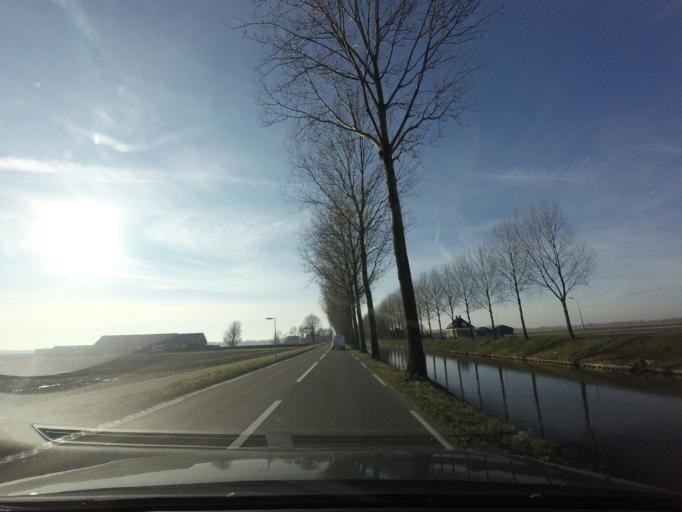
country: NL
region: North Holland
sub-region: Gemeente Haarlemmermeer
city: Hoofddorp
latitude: 52.3232
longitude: 4.7184
